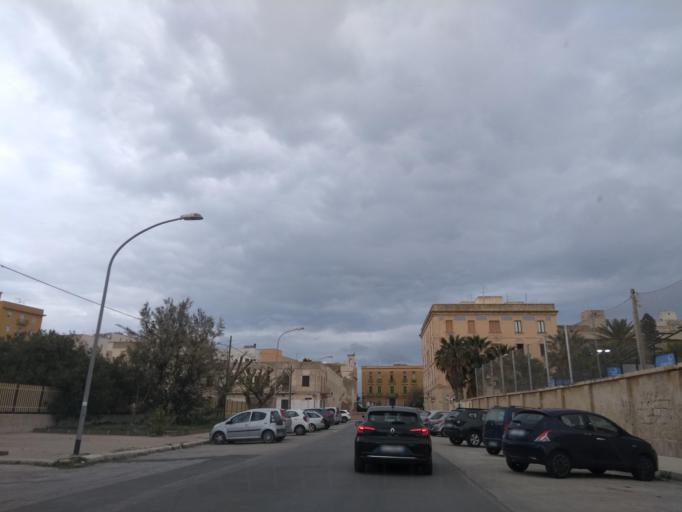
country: IT
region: Sicily
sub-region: Trapani
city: Trapani
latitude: 38.0154
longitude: 12.5011
